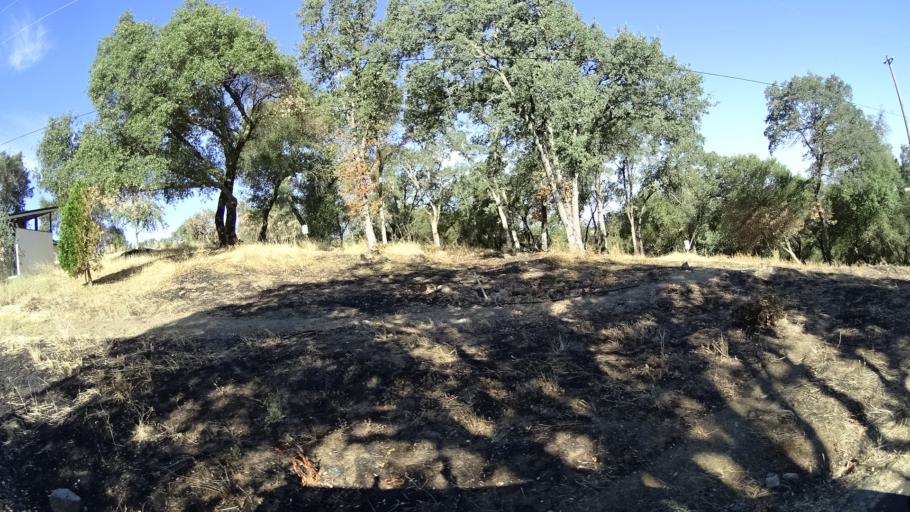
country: US
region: California
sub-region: Calaveras County
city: San Andreas
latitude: 38.1882
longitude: -120.6672
